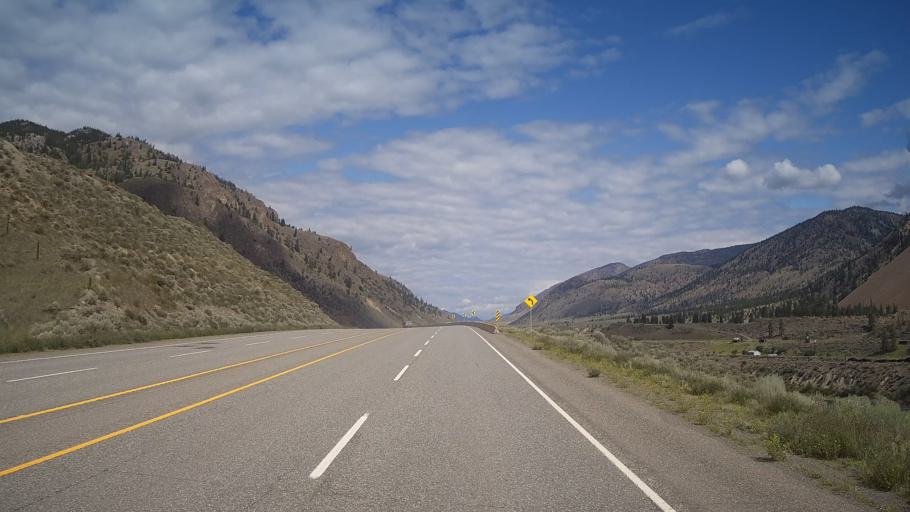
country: CA
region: British Columbia
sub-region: Thompson-Nicola Regional District
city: Ashcroft
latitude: 50.5150
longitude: -121.2815
